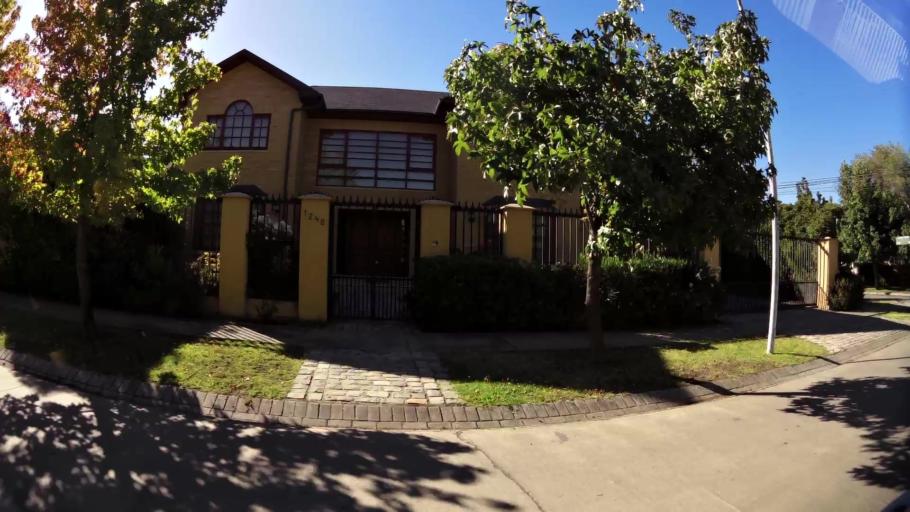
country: CL
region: O'Higgins
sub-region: Provincia de Cachapoal
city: Rancagua
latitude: -34.1920
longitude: -70.7173
